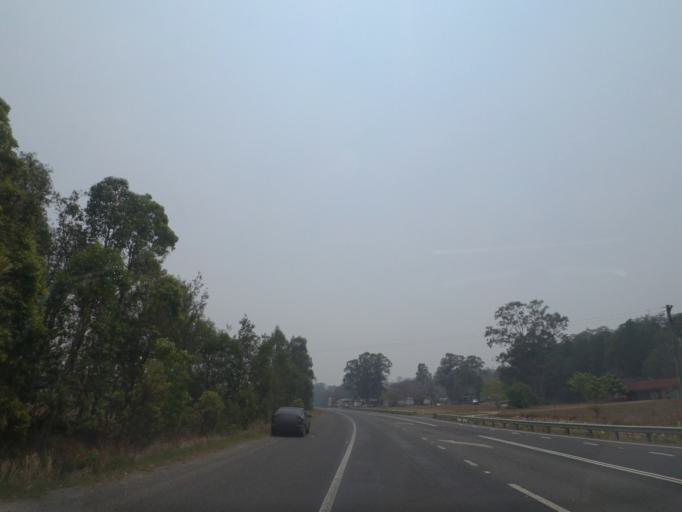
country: AU
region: New South Wales
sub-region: Clarence Valley
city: Maclean
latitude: -29.5628
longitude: 153.1477
